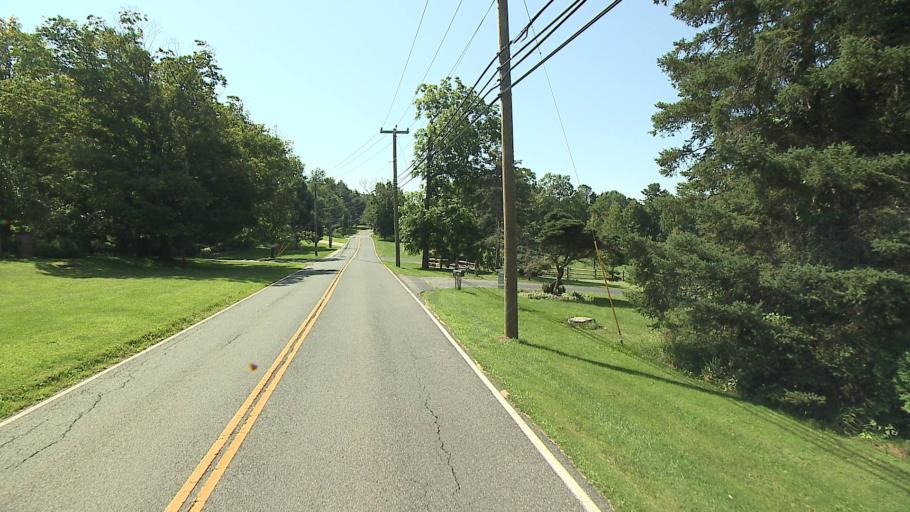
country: US
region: Connecticut
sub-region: Litchfield County
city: Kent
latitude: 41.8714
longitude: -73.4774
